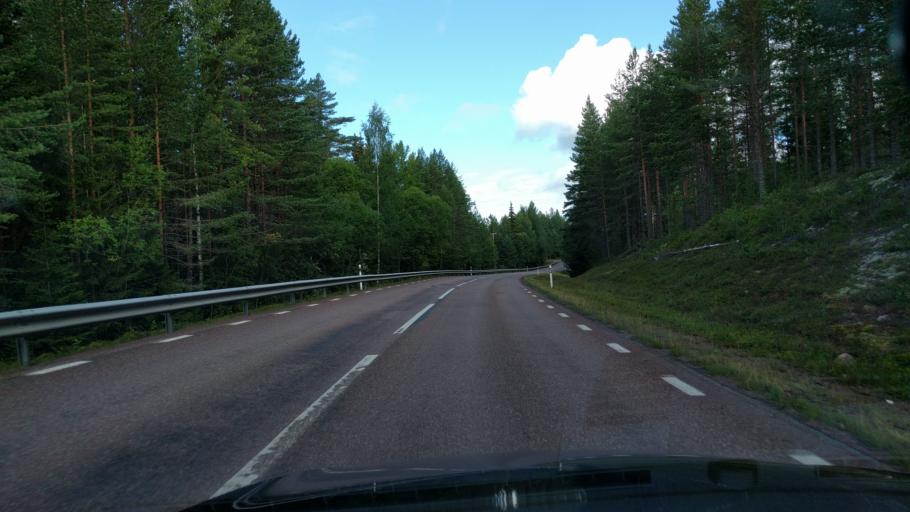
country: SE
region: Dalarna
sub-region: Mora Kommun
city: Mora
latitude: 61.0794
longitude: 14.3336
